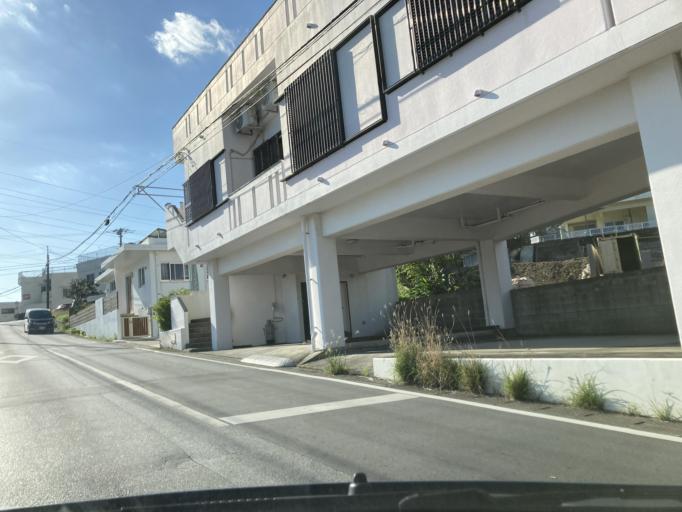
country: JP
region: Okinawa
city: Ginowan
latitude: 26.2194
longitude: 127.7535
